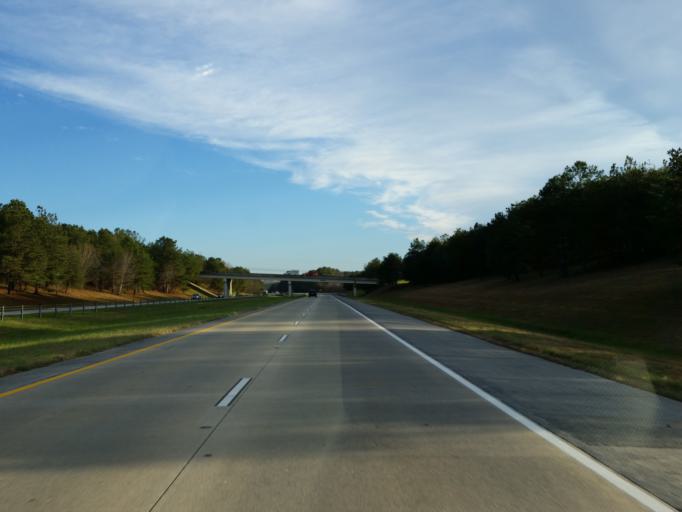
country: US
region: Georgia
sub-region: Cherokee County
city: Ball Ground
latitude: 34.2990
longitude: -84.4261
